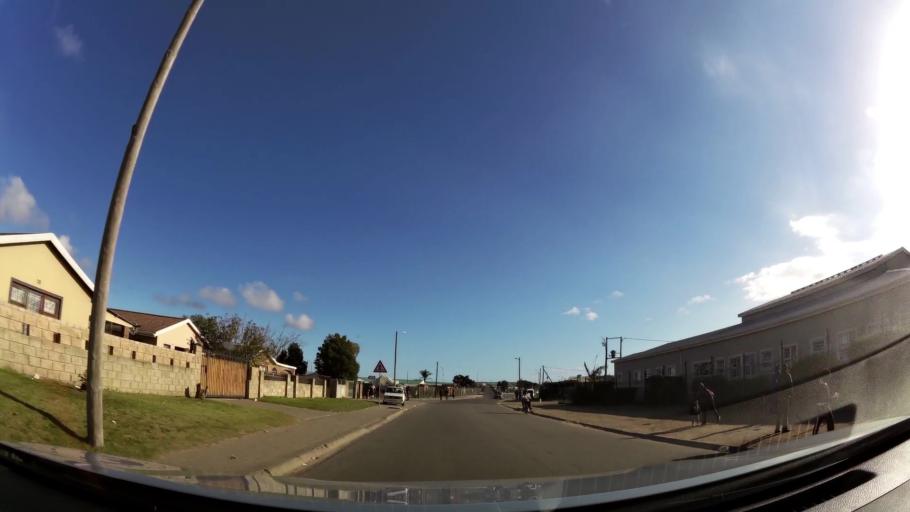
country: ZA
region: Western Cape
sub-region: Eden District Municipality
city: George
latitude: -33.9918
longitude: 22.4761
